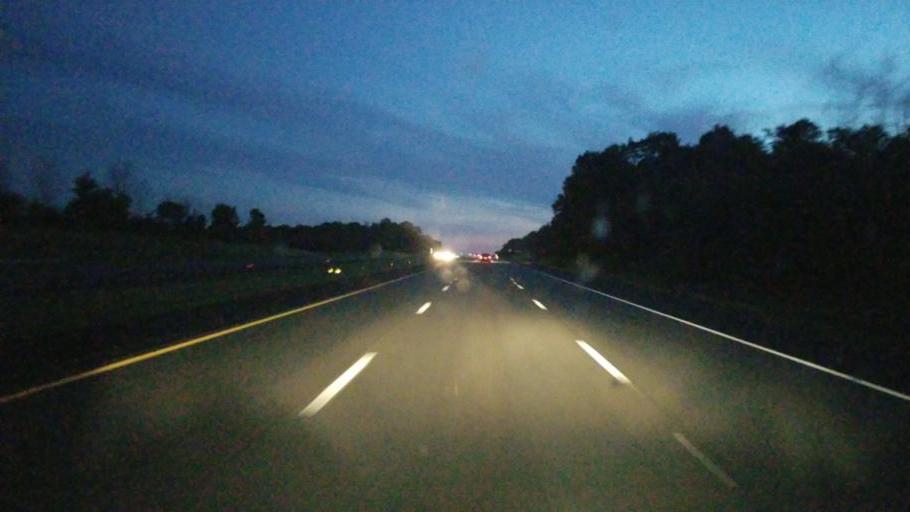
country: US
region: Ohio
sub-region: Medina County
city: Westfield Center
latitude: 41.0112
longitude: -81.9409
